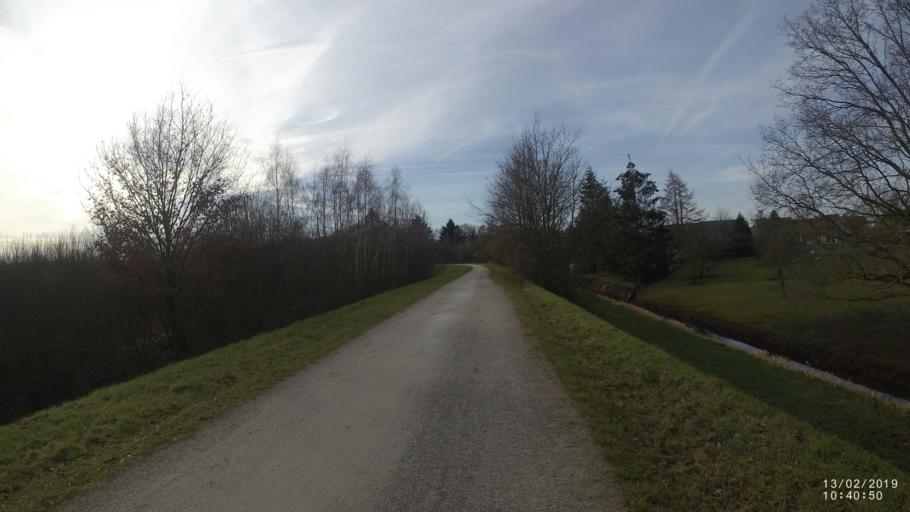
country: BE
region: Flanders
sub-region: Provincie Vlaams-Brabant
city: Diest
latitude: 50.9720
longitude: 5.0746
